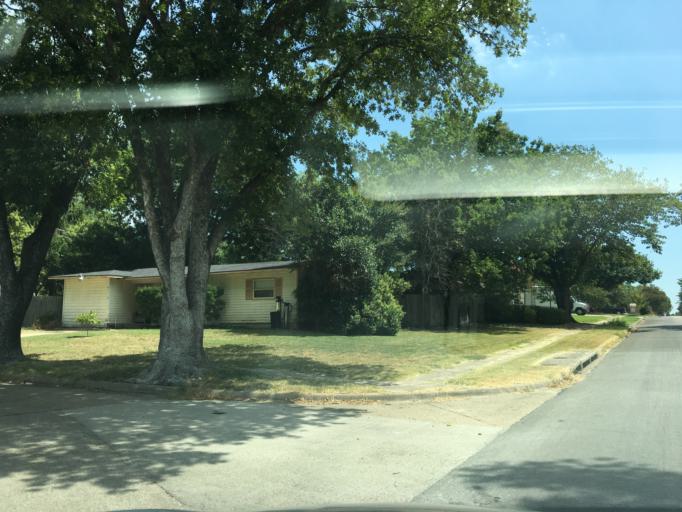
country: US
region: Texas
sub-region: Dallas County
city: Garland
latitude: 32.8600
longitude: -96.6821
